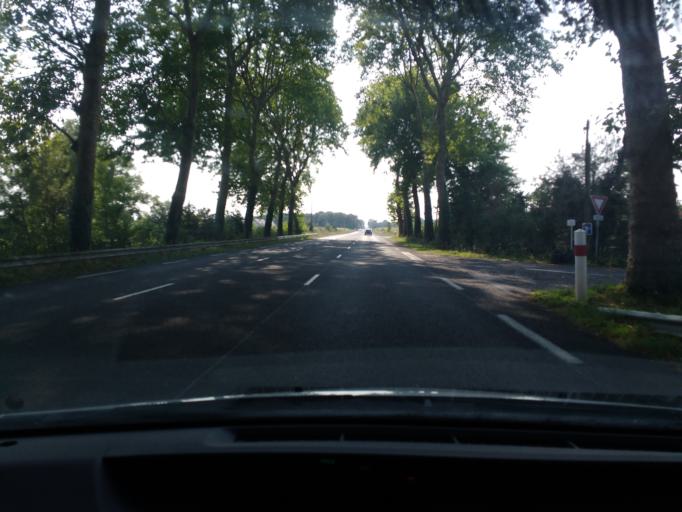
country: FR
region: Pays de la Loire
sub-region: Departement de la Sarthe
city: La Fleche
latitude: 47.6937
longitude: -0.1219
